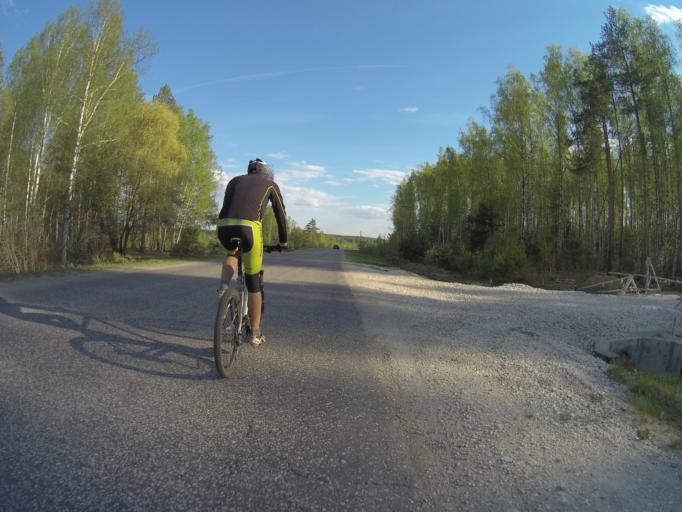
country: RU
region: Vladimir
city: Sudogda
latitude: 56.0927
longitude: 40.7861
